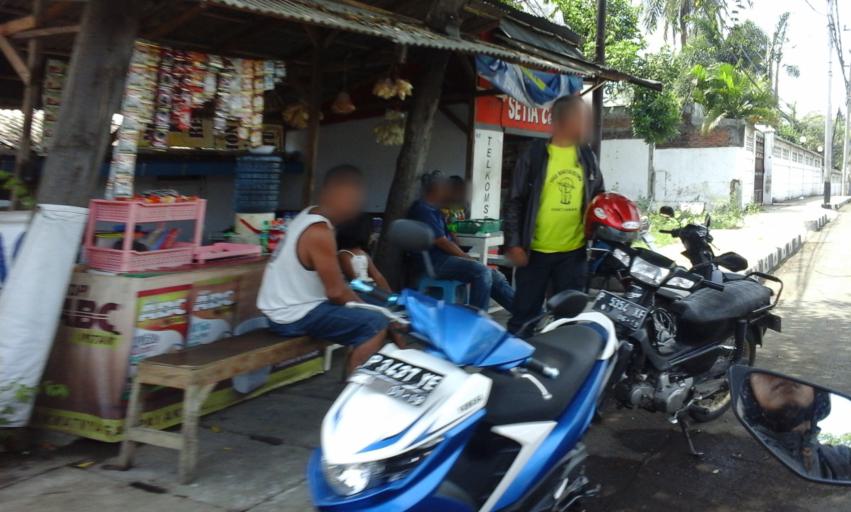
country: ID
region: East Java
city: Klatakan
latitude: -8.1777
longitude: 114.3831
